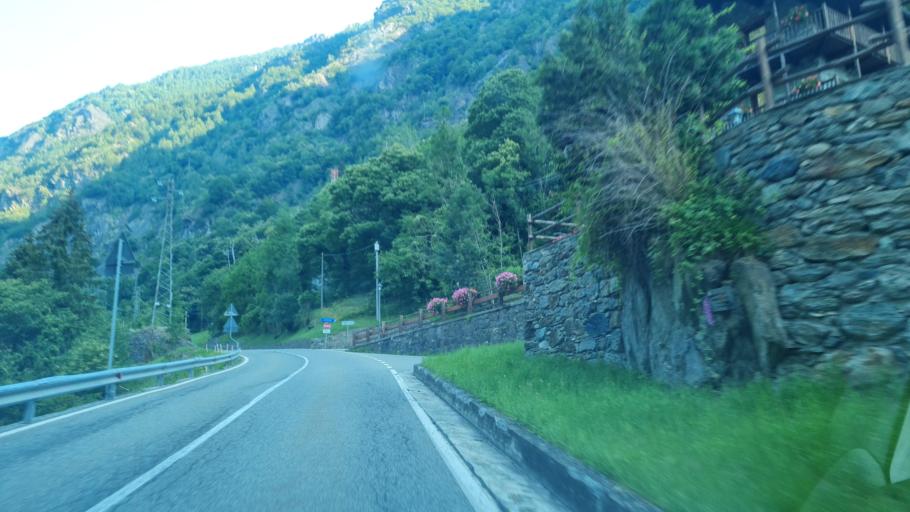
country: IT
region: Aosta Valley
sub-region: Valle d'Aosta
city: Pont-Bozet
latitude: 45.6132
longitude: 7.6799
